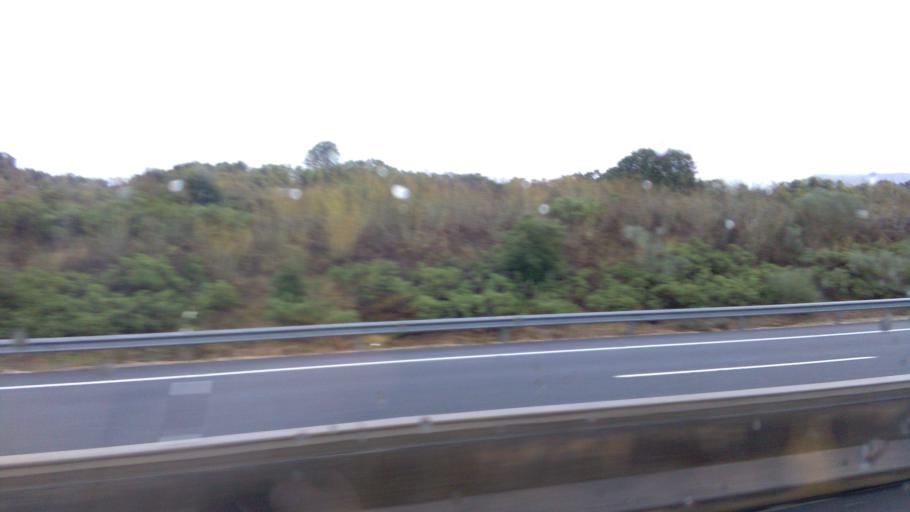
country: ES
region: Extremadura
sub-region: Provincia de Caceres
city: Casas de Miravete
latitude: 39.7728
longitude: -5.7378
